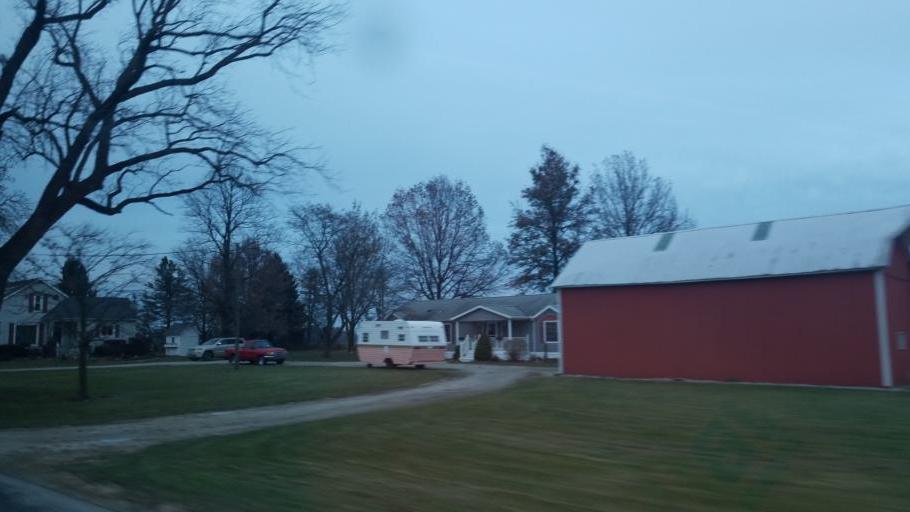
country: US
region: Indiana
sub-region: Adams County
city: Decatur
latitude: 40.7816
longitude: -85.0146
